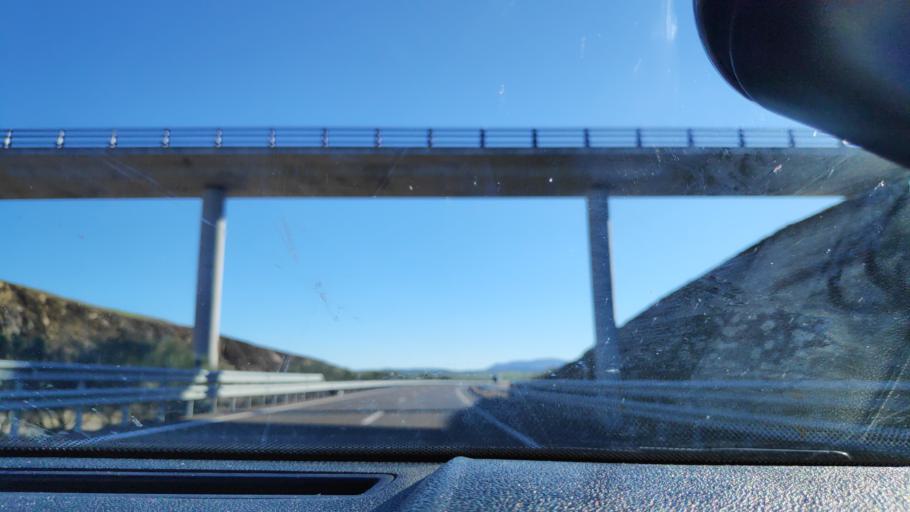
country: ES
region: Extremadura
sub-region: Provincia de Badajoz
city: Fuente de Cantos
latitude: 38.1895
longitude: -6.2797
